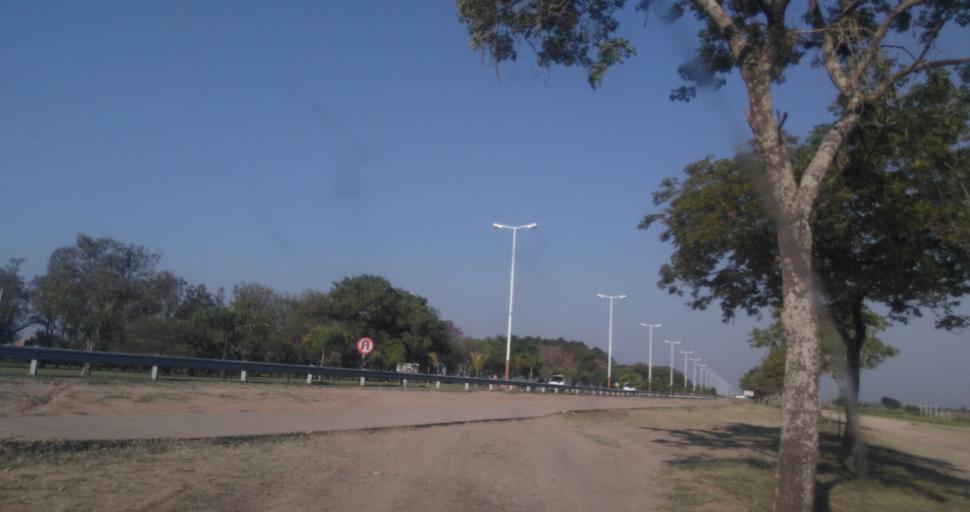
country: AR
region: Chaco
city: Fontana
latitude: -27.4405
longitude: -59.0322
